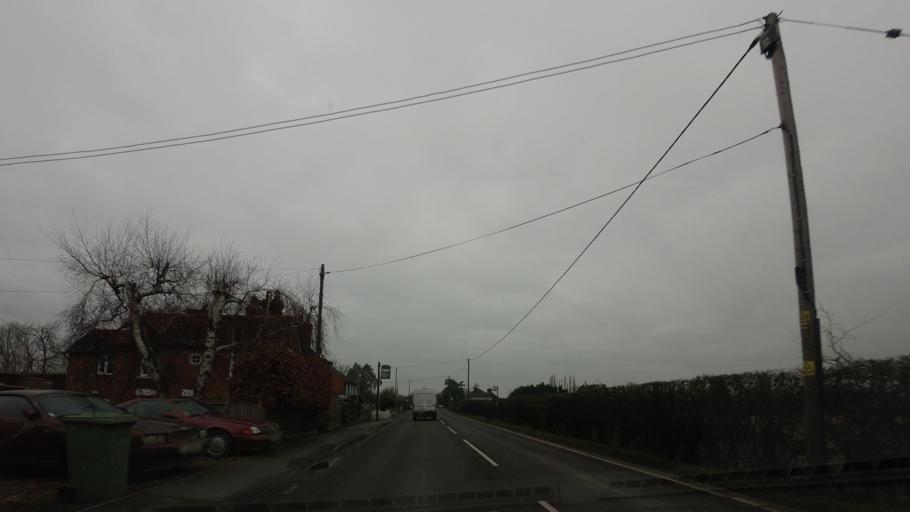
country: GB
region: England
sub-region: Kent
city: Staplehurst
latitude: 51.1368
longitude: 0.5561
